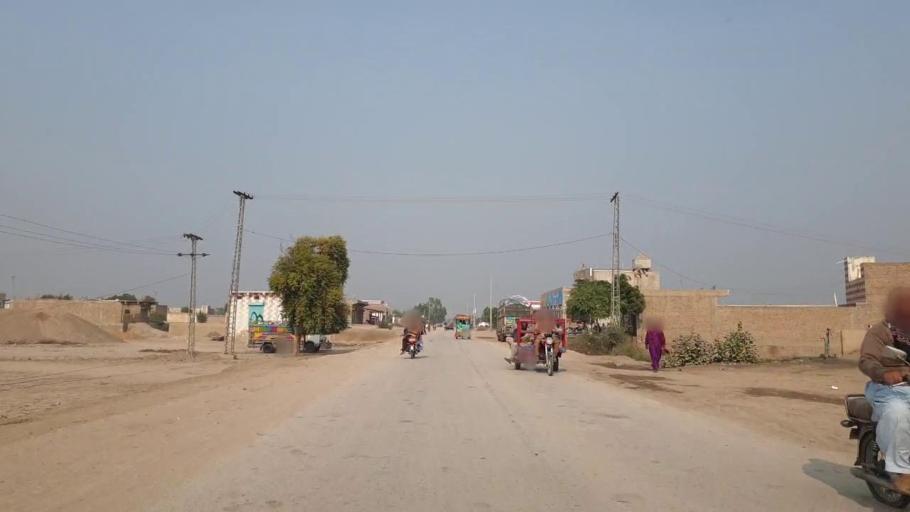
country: PK
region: Sindh
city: Bhan
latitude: 26.5651
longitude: 67.7239
